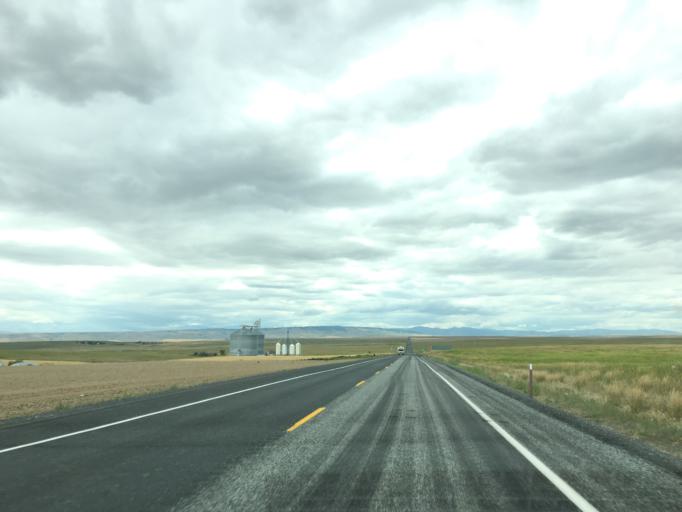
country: US
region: Washington
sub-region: Douglas County
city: Waterville
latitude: 47.6126
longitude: -119.8054
